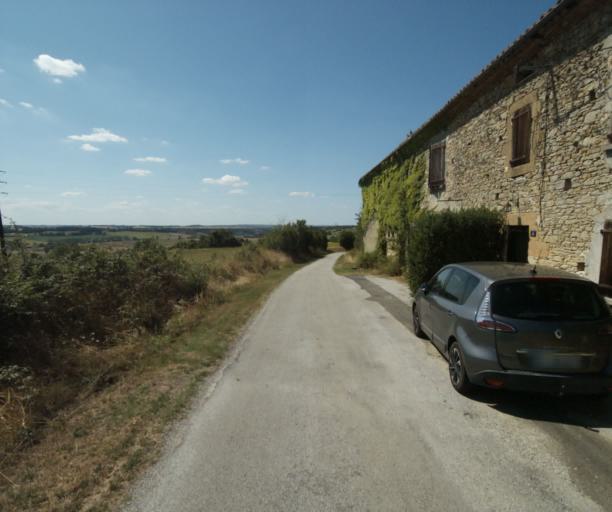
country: FR
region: Midi-Pyrenees
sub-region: Departement de la Haute-Garonne
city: Saint-Felix-Lauragais
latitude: 43.4904
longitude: 1.8954
